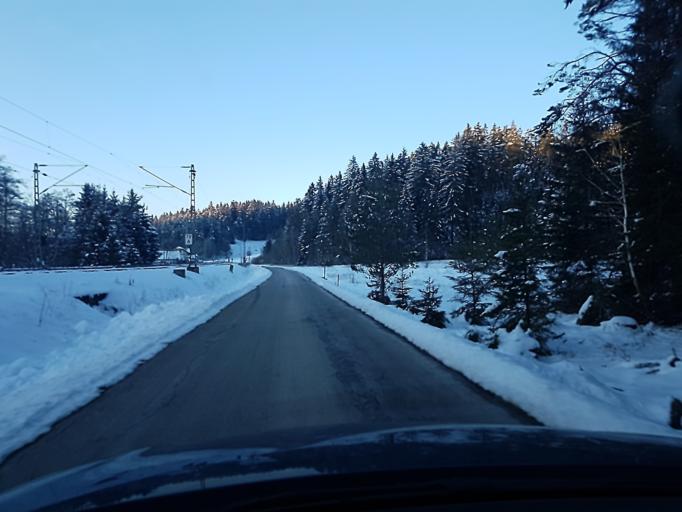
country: DE
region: Baden-Wuerttemberg
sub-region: Freiburg Region
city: Monchweiler
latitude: 48.0870
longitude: 8.4049
